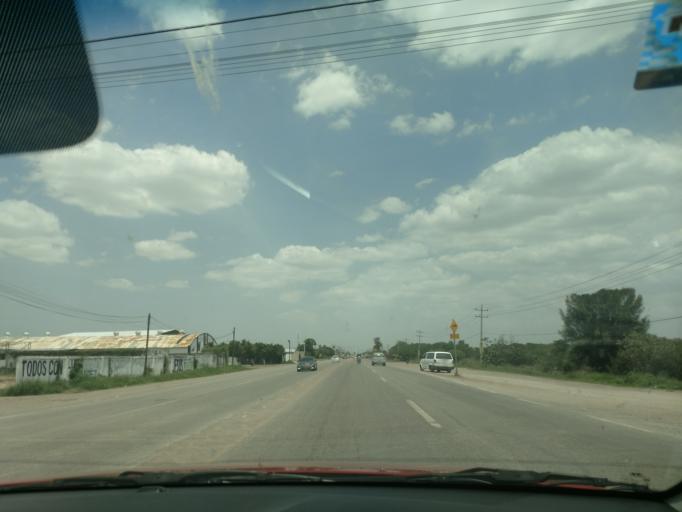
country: MX
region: San Luis Potosi
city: Ciudad Fernandez
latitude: 21.9394
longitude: -100.0359
